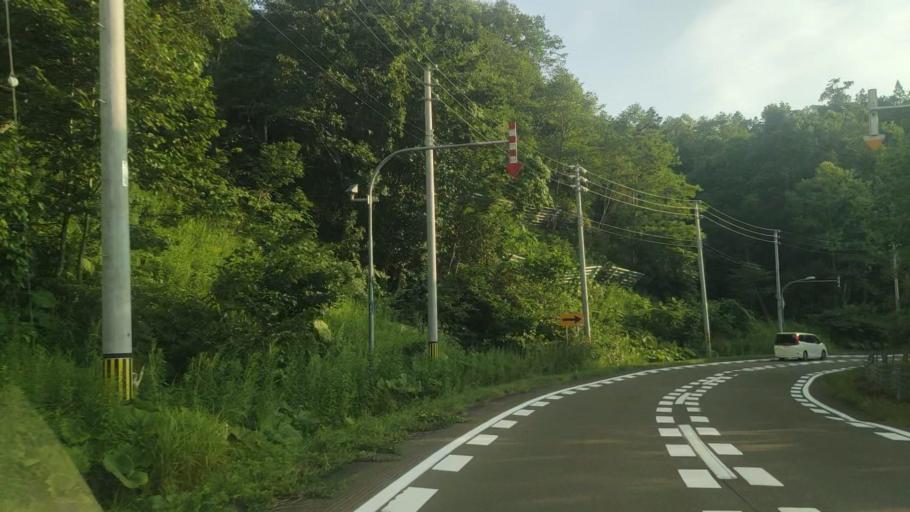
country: JP
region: Hokkaido
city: Bibai
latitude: 43.1685
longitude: 142.0742
